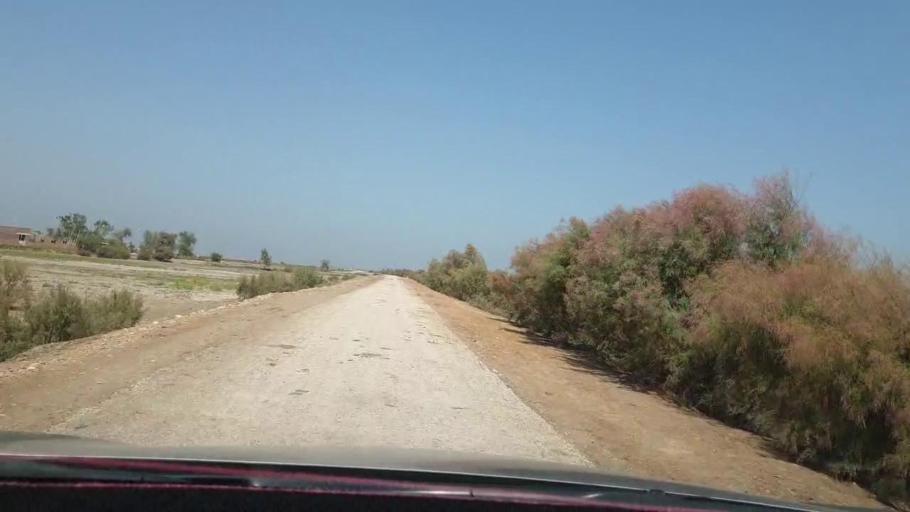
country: PK
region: Sindh
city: Warah
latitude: 27.5244
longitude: 67.7093
